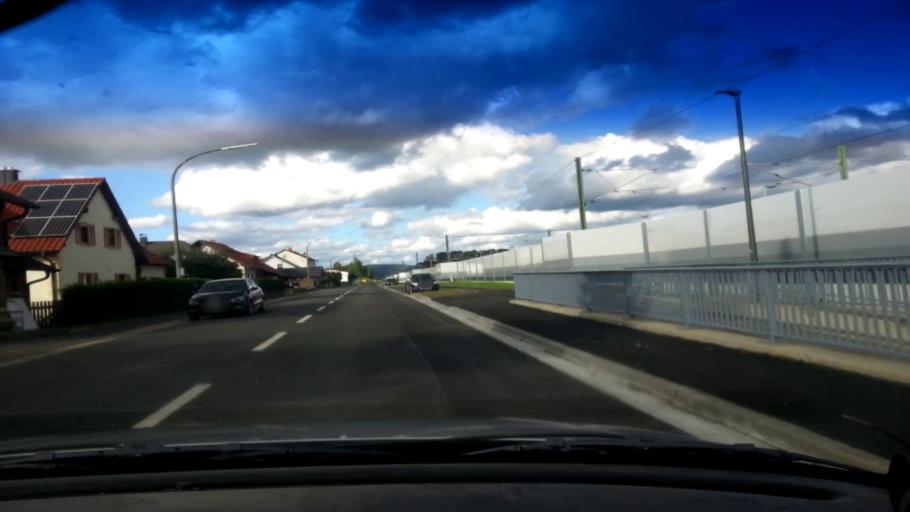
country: DE
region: Bavaria
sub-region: Upper Franconia
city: Ebensfeld
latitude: 50.0683
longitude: 10.9541
